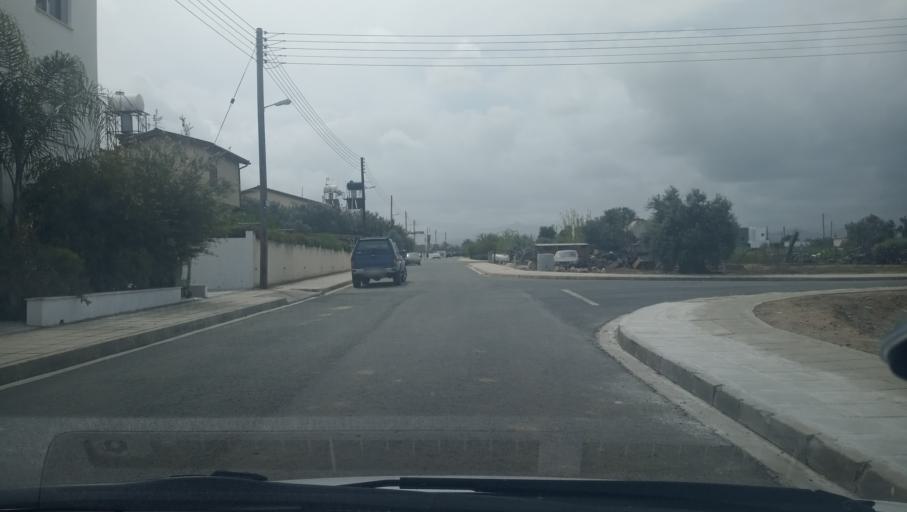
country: CY
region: Lefkosia
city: Pano Deftera
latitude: 35.0758
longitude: 33.2694
